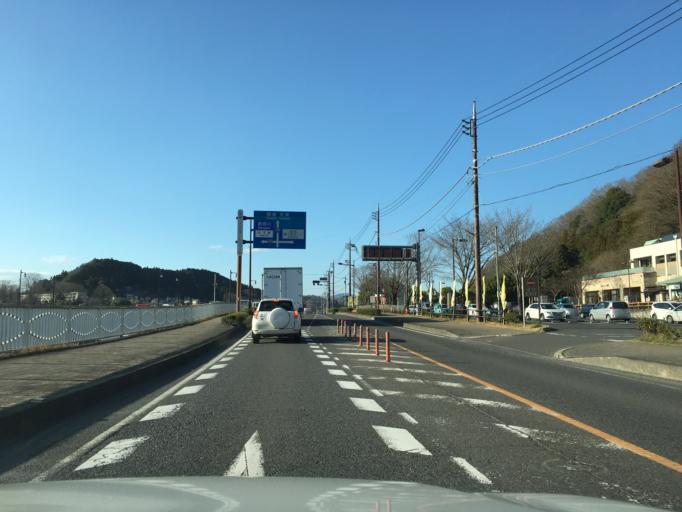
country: JP
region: Ibaraki
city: Daigo
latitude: 36.7677
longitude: 140.3589
